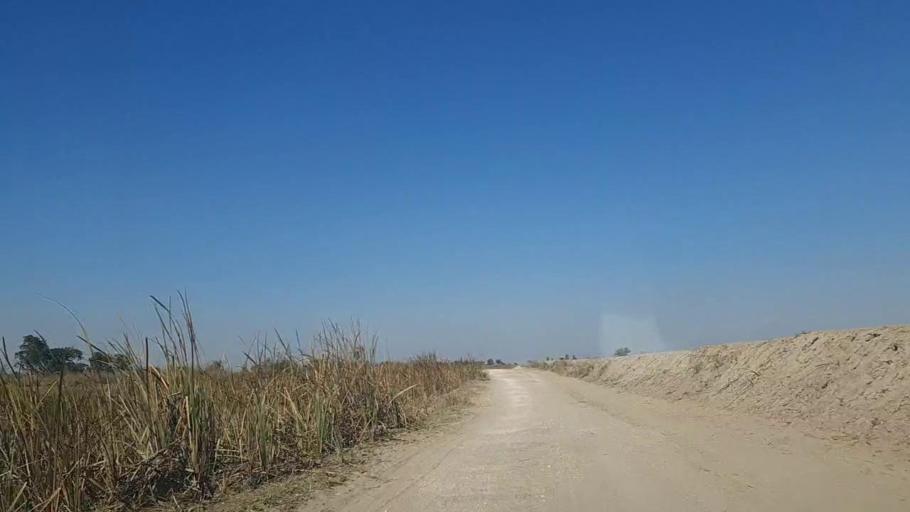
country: PK
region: Sindh
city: Sanghar
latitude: 26.2129
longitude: 68.9293
